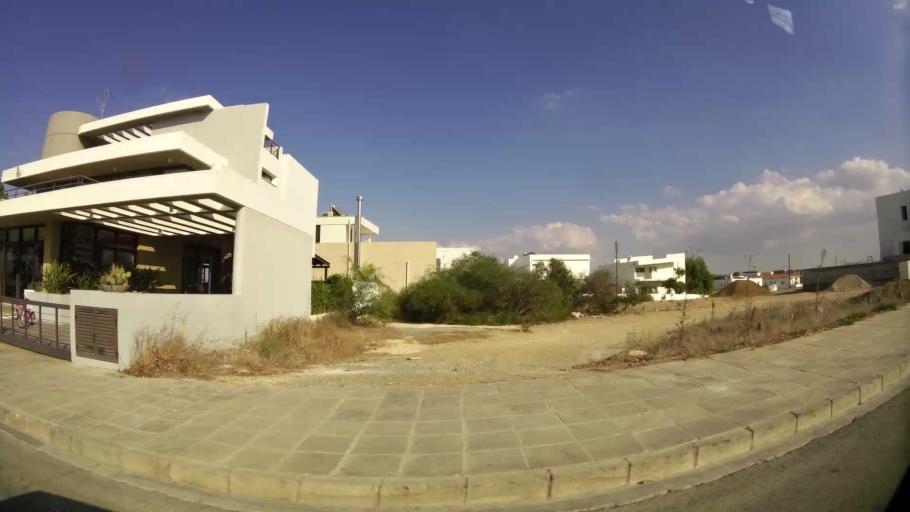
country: CY
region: Lefkosia
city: Kato Deftera
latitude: 35.1397
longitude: 33.2941
